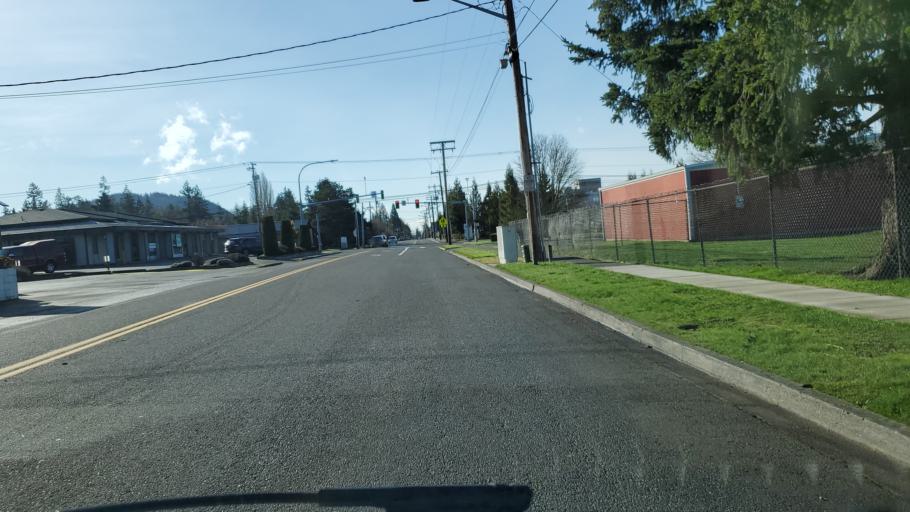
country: US
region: Washington
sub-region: Skagit County
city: Mount Vernon
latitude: 48.4219
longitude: -122.3230
